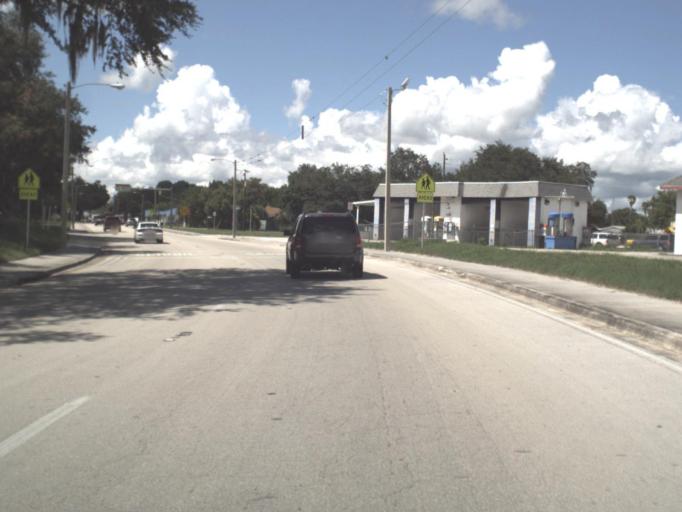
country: US
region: Florida
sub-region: DeSoto County
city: Arcadia
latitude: 27.2133
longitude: -81.8509
